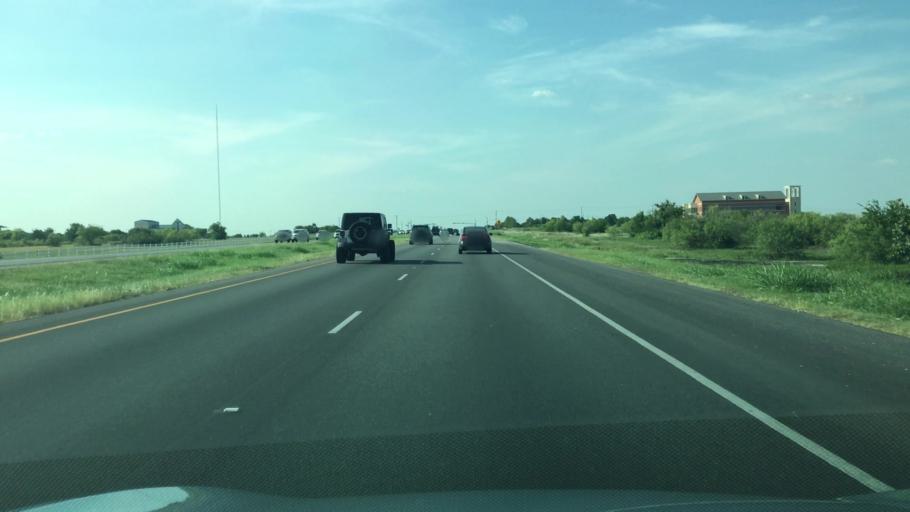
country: US
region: Texas
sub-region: Hays County
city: Kyle
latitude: 30.0220
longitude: -97.8721
